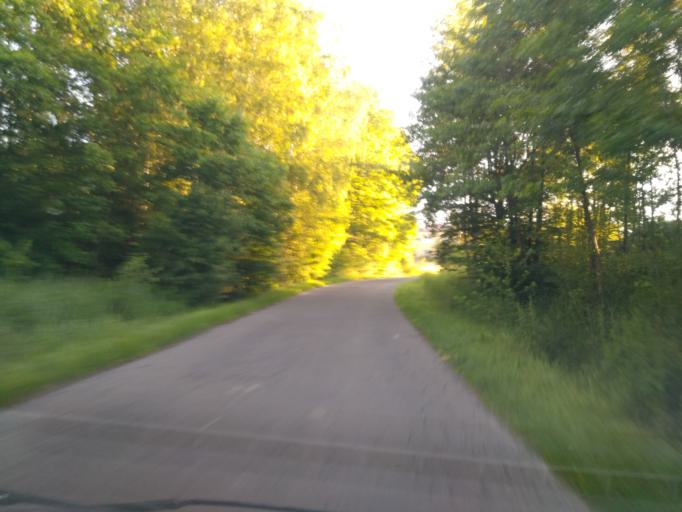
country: PL
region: Subcarpathian Voivodeship
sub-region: Powiat strzyzowski
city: Polomia
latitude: 49.9006
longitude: 21.8850
